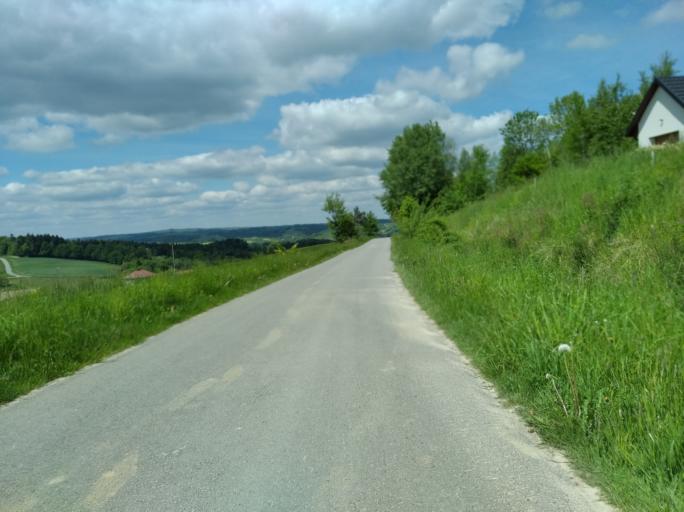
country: PL
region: Subcarpathian Voivodeship
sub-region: Powiat ropczycko-sedziszowski
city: Wielopole Skrzynskie
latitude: 49.9249
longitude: 21.6050
